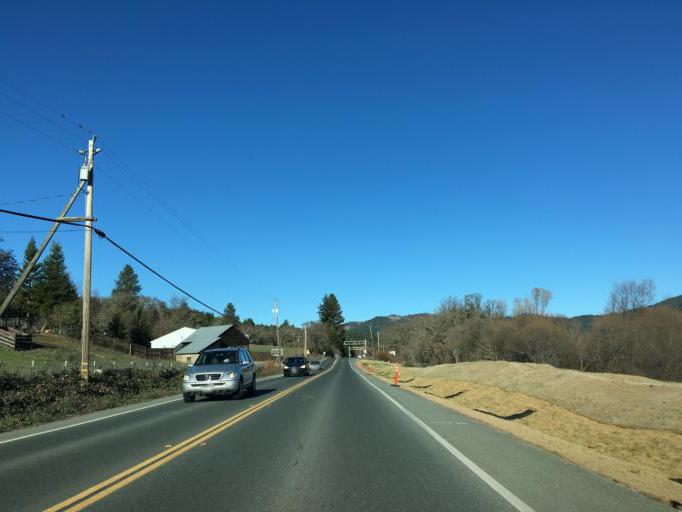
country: US
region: California
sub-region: Mendocino County
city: Willits
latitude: 39.4380
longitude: -123.3566
